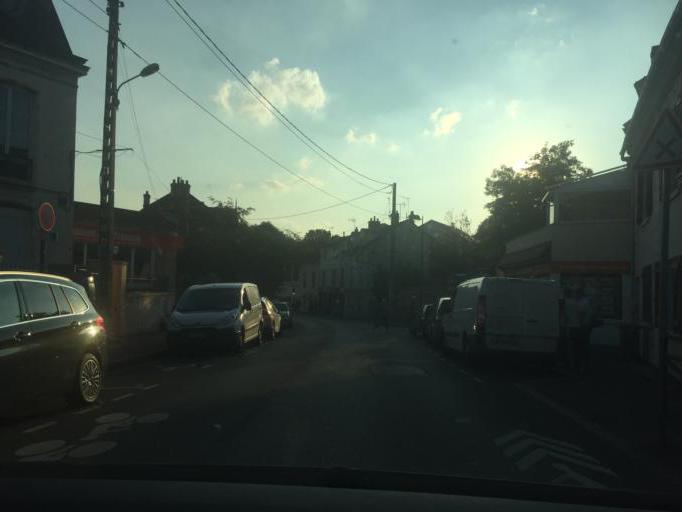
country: FR
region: Ile-de-France
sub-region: Departement de l'Essonne
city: Orsay
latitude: 48.7014
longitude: 2.1891
